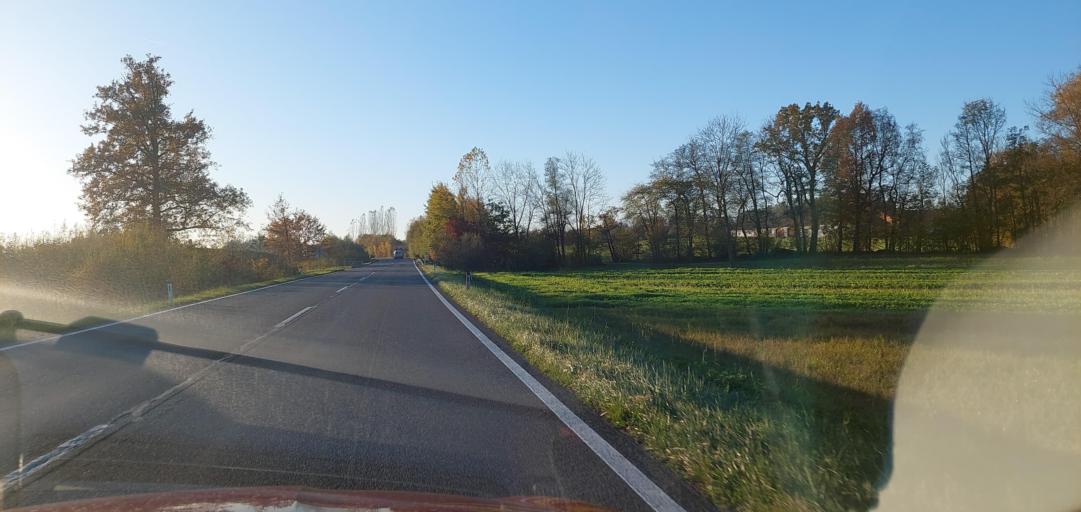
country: AT
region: Upper Austria
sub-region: Politischer Bezirk Vocklabruck
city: Wolfsegg am Hausruck
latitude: 48.2194
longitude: 13.7057
